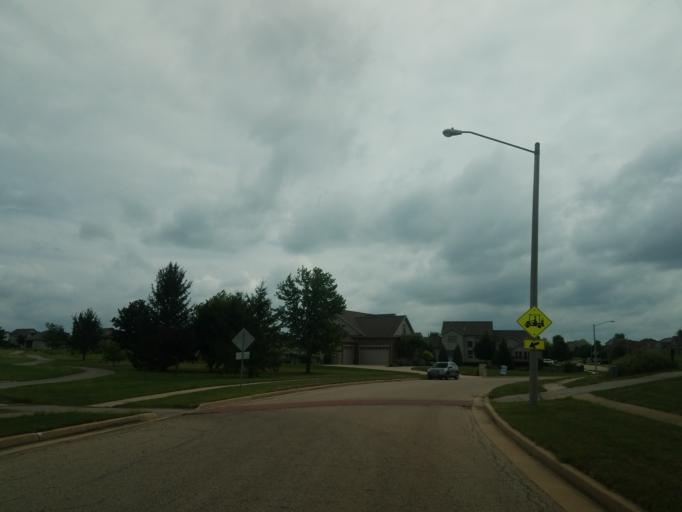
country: US
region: Illinois
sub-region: McLean County
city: Twin Grove
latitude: 40.4421
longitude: -89.0418
